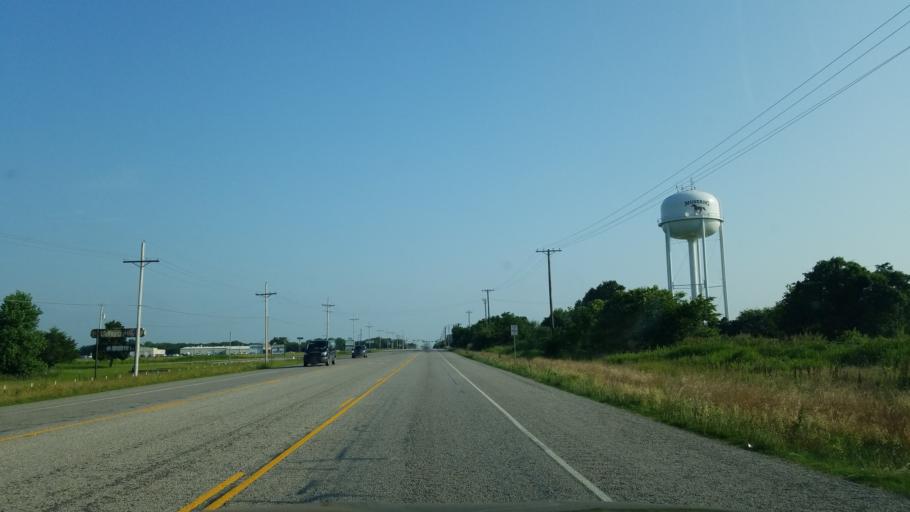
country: US
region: Texas
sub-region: Denton County
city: Pilot Point
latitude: 33.3727
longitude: -96.9636
